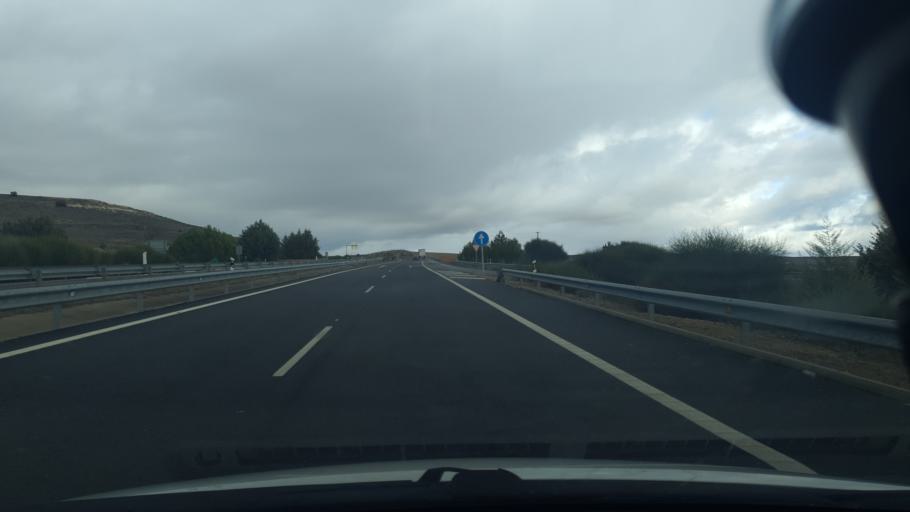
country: ES
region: Castille and Leon
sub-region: Provincia de Segovia
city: Cuellar
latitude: 41.3867
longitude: -4.2953
